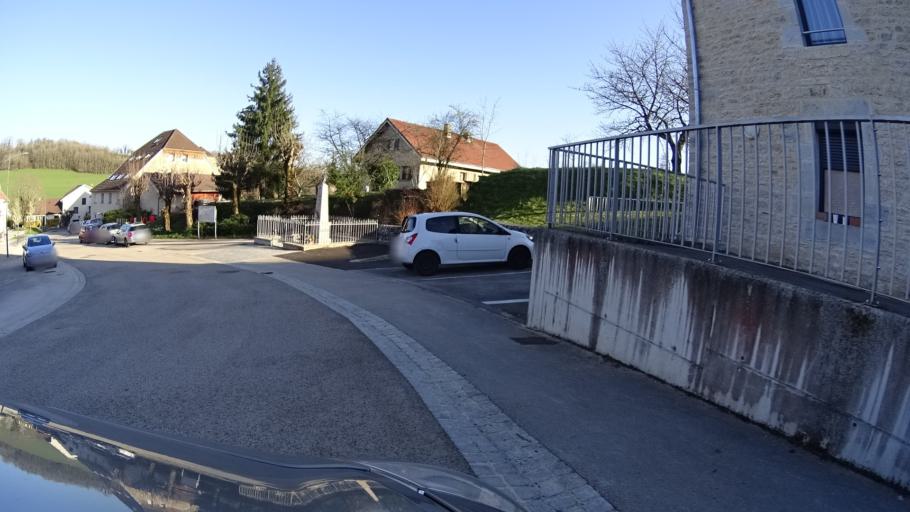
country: FR
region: Franche-Comte
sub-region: Departement du Doubs
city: Beure
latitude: 47.1846
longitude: 5.9899
